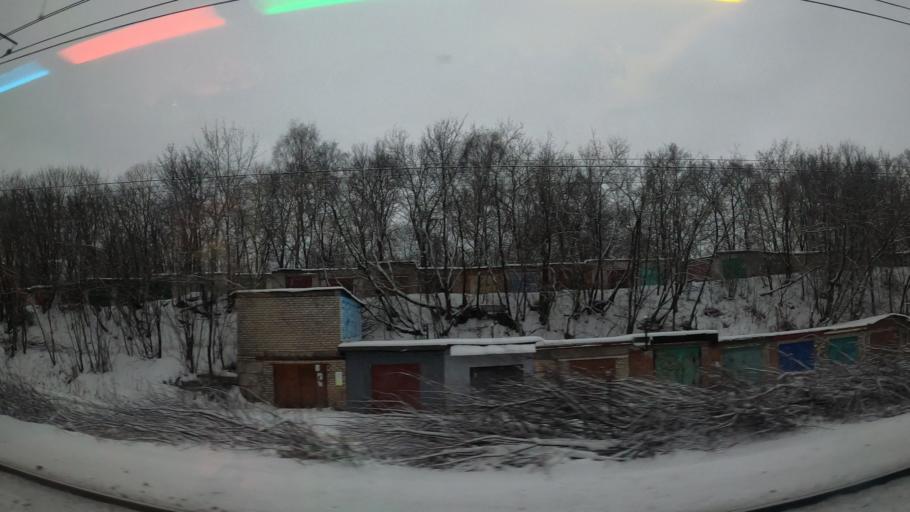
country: RU
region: Vladimir
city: Aleksandrov
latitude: 56.4054
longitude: 38.7204
